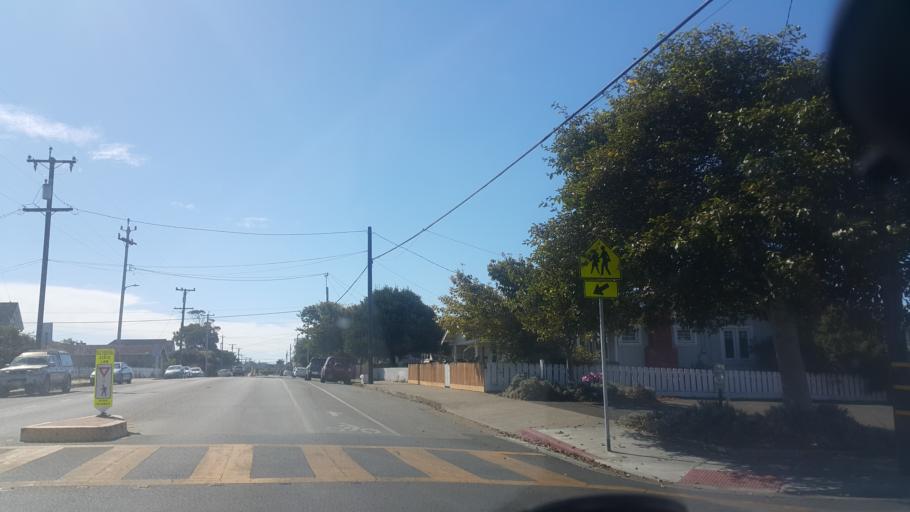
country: US
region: California
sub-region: Mendocino County
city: Fort Bragg
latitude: 39.4442
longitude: -123.7981
